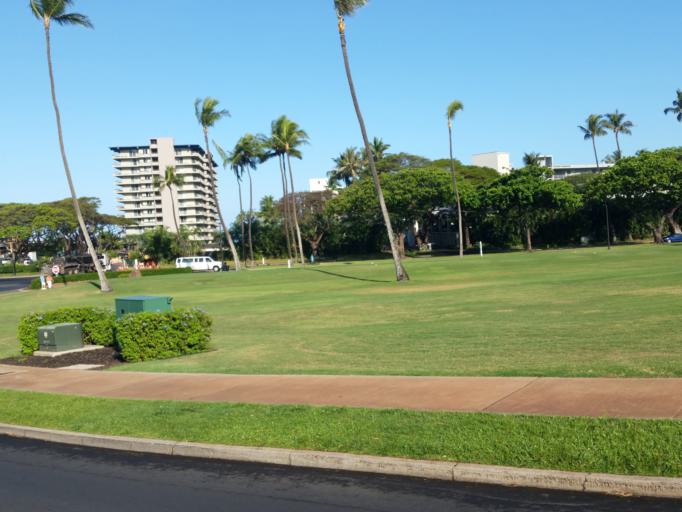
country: US
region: Hawaii
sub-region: Maui County
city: Ka'anapali
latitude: 20.9228
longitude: -156.6920
